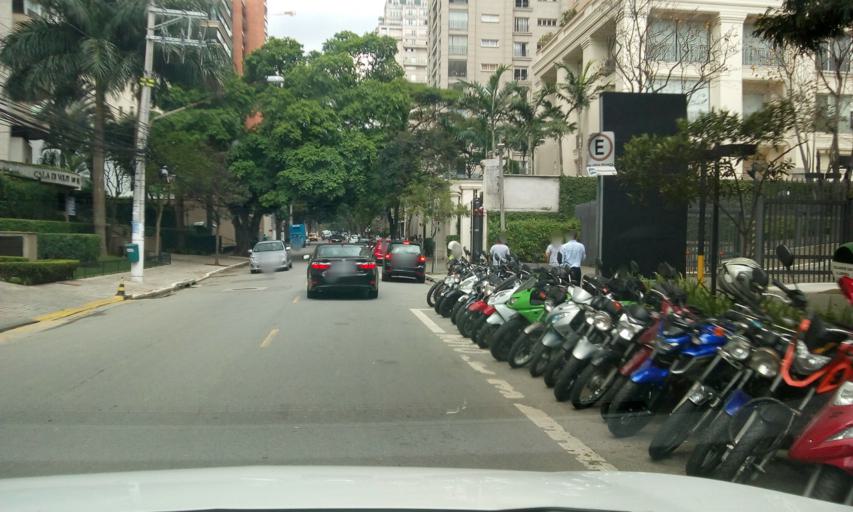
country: BR
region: Sao Paulo
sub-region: Sao Paulo
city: Sao Paulo
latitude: -23.5899
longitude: -46.6867
